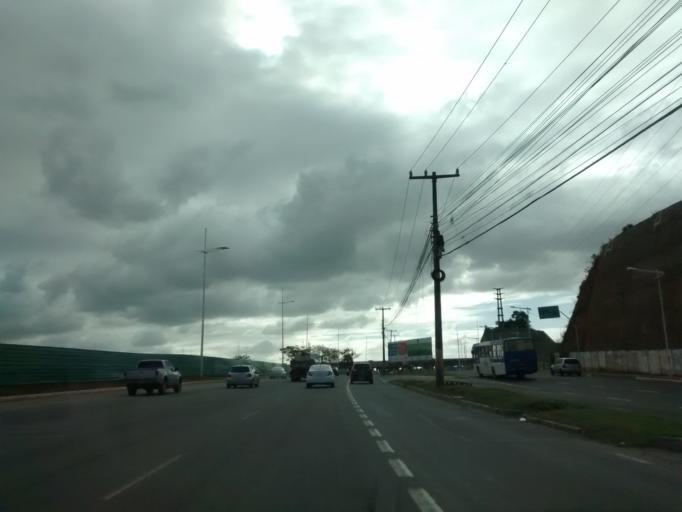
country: BR
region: Bahia
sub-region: Lauro De Freitas
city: Lauro de Freitas
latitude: -12.9276
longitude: -38.3851
